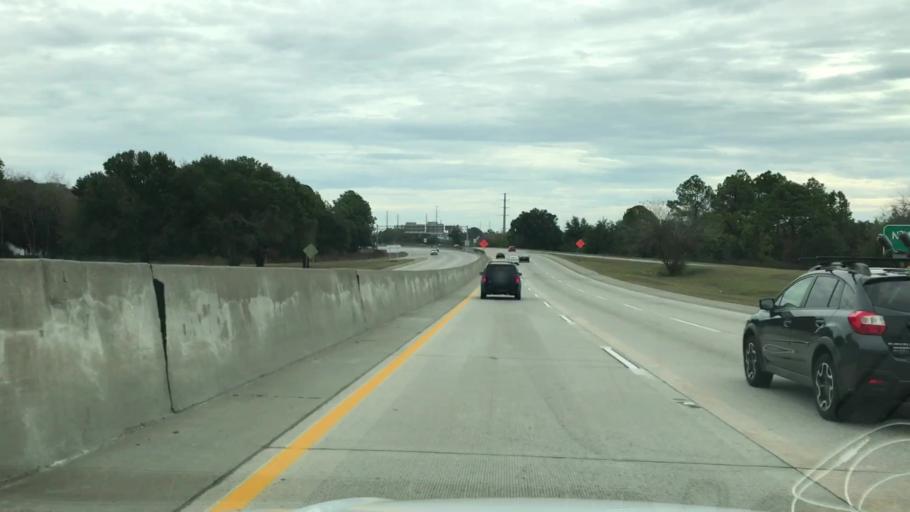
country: US
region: South Carolina
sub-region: Charleston County
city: North Charleston
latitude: 32.8425
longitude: -79.9786
